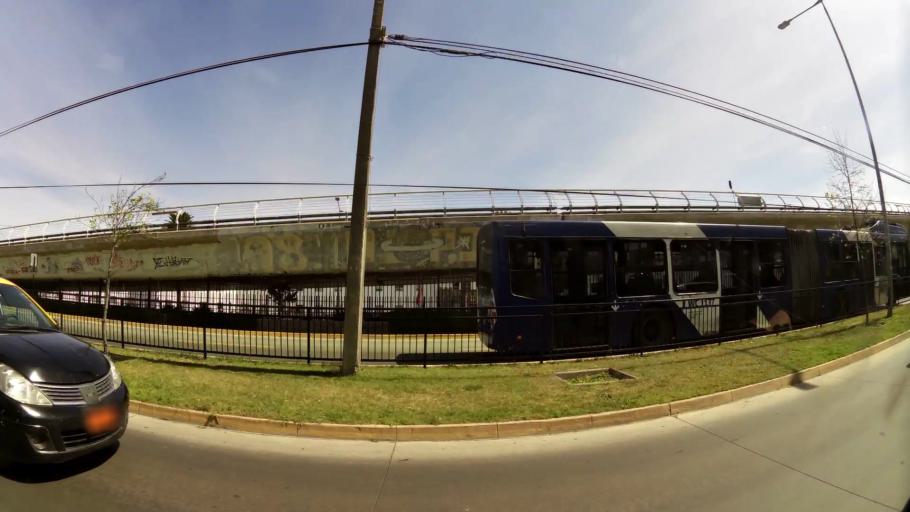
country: CL
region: Santiago Metropolitan
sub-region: Provincia de Cordillera
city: Puente Alto
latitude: -33.5951
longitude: -70.5786
